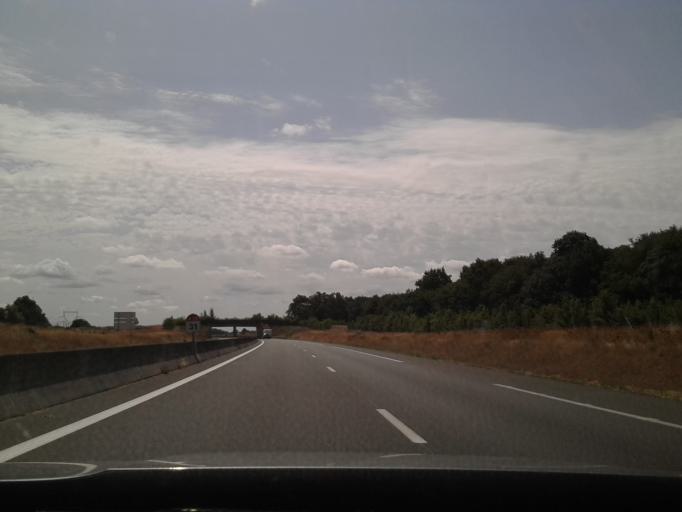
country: FR
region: Centre
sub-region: Departement d'Indre-et-Loire
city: Rouziers-de-Touraine
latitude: 47.5256
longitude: 0.6228
